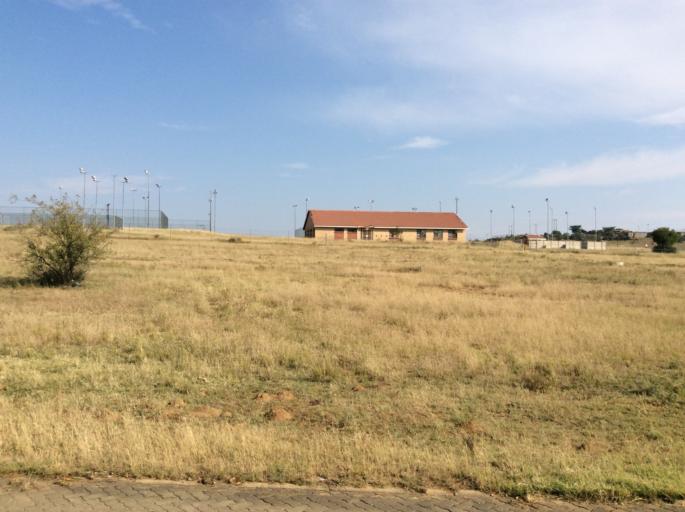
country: LS
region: Mafeteng
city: Mafeteng
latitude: -29.7226
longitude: 27.0178
